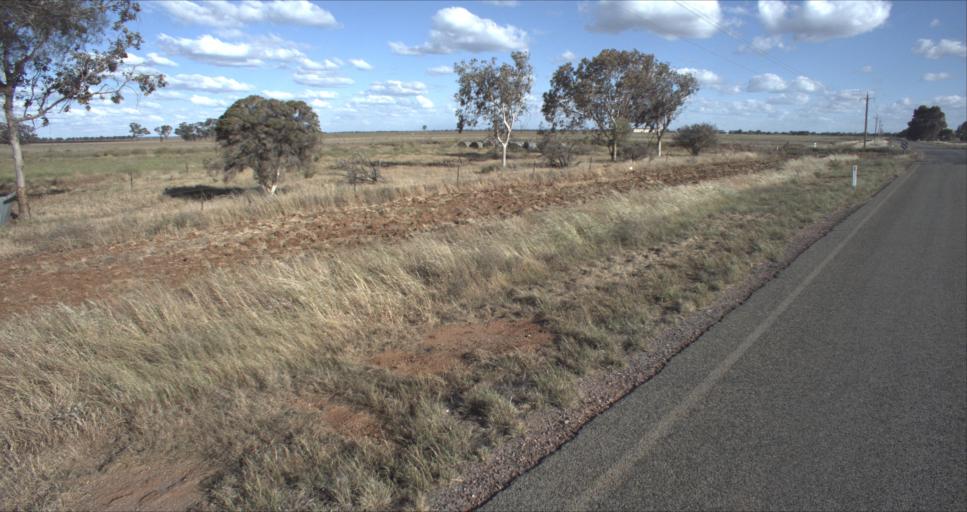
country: AU
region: New South Wales
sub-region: Leeton
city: Leeton
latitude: -34.5369
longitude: 146.2804
